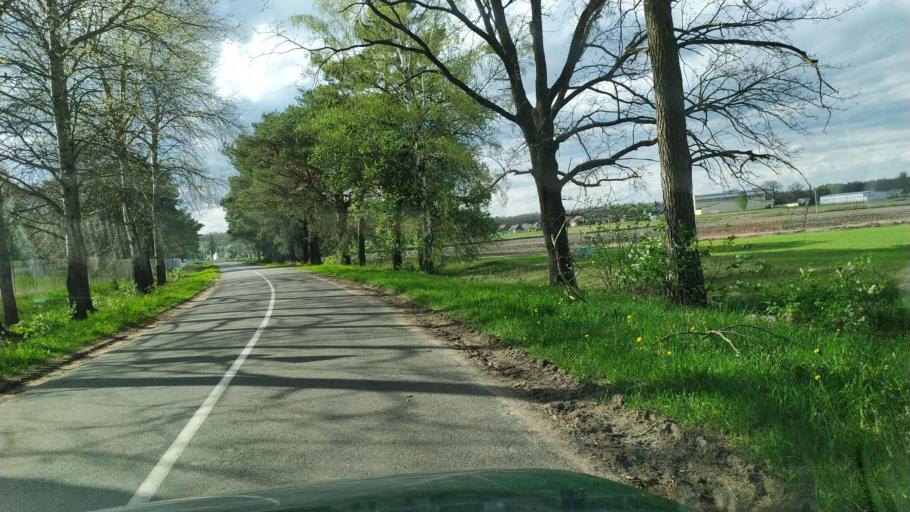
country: BY
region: Brest
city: Pruzhany
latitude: 52.6976
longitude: 24.2193
